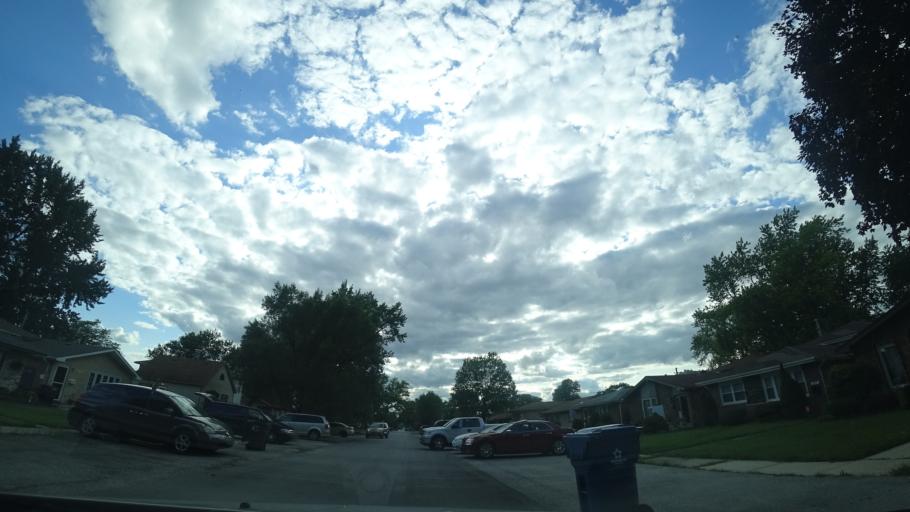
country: US
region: Illinois
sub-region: Cook County
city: Merrionette Park
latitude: 41.6822
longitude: -87.7139
